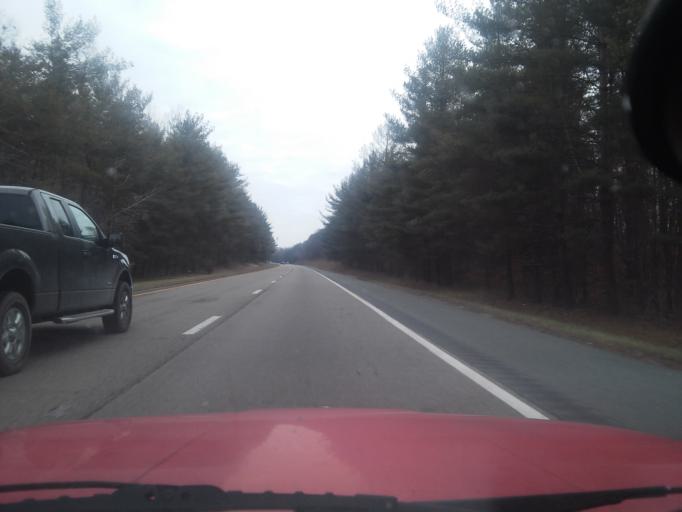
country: US
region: Virginia
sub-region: Fluvanna County
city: Palmyra
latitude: 37.9618
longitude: -78.1766
